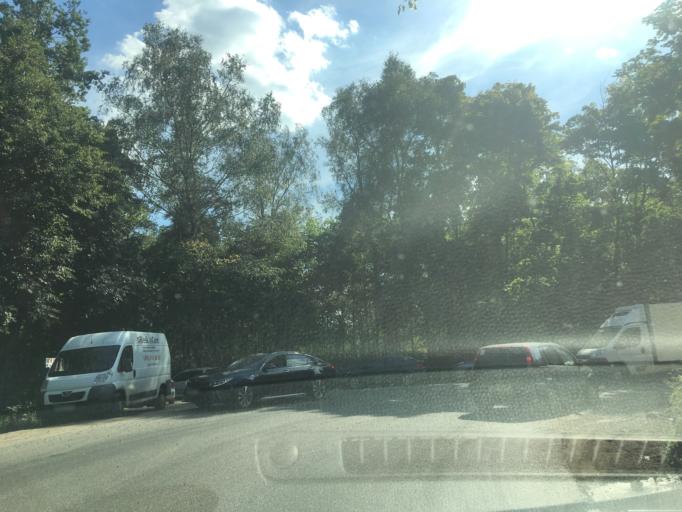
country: RU
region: Moscow
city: Zagor'ye
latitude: 55.5280
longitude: 37.6631
